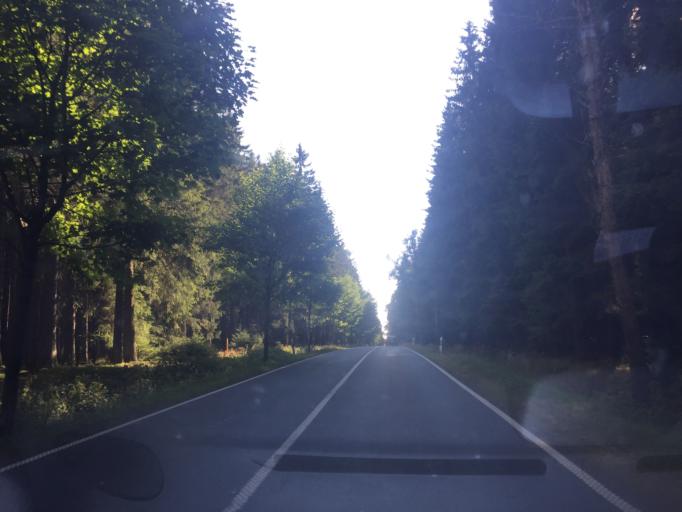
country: DE
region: Lower Saxony
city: Braunlage
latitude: 51.7334
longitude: 10.6324
